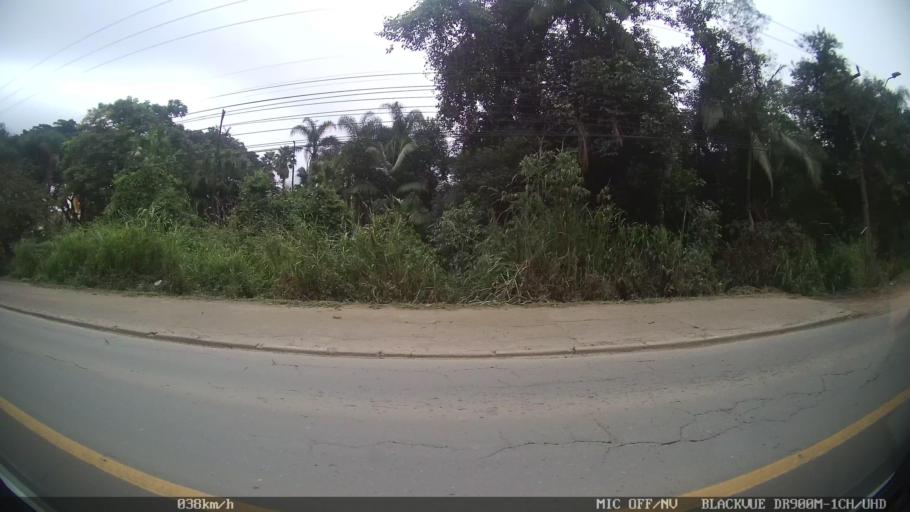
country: BR
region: Santa Catarina
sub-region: Joinville
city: Joinville
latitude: -26.2510
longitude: -48.8748
